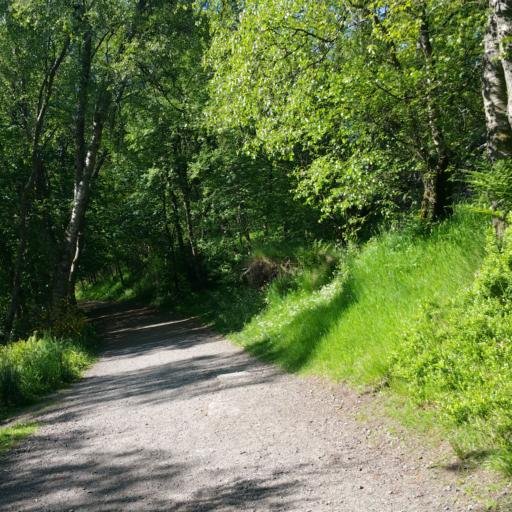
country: GB
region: Scotland
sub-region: East Dunbartonshire
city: Milngavie
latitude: 55.9565
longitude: -4.3300
